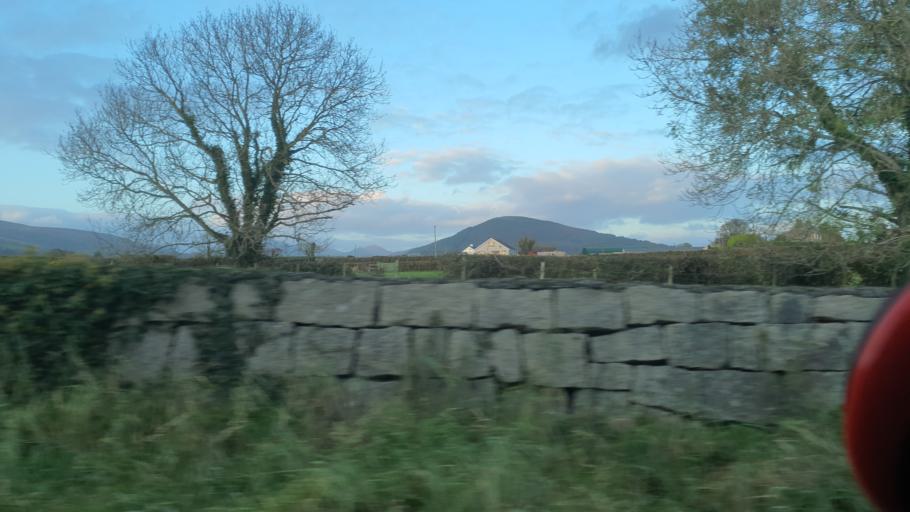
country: GB
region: Northern Ireland
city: Kilkeel
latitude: 54.0615
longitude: -6.0913
